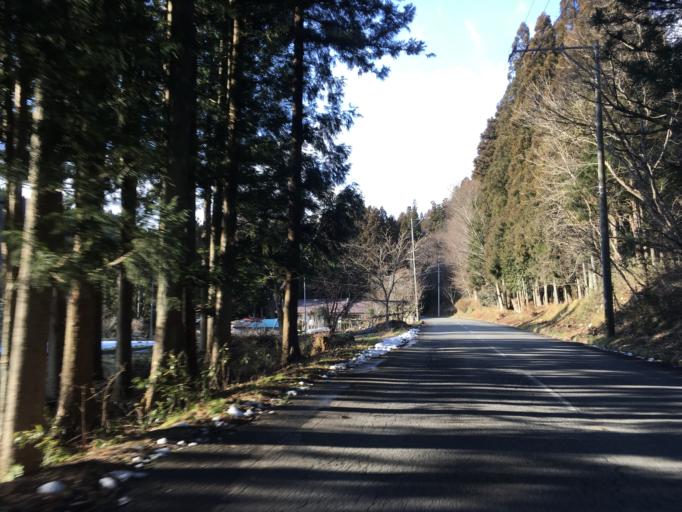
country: JP
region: Miyagi
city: Furukawa
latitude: 38.8029
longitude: 140.8313
